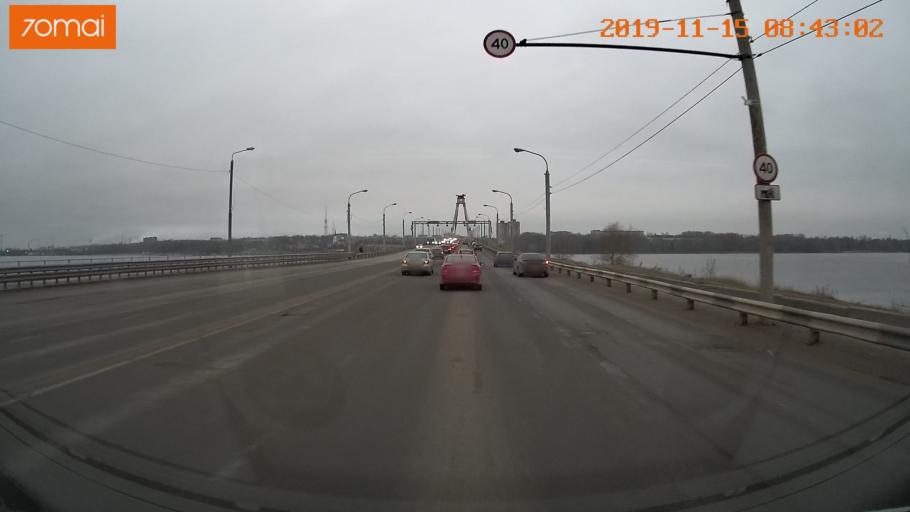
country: RU
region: Vologda
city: Cherepovets
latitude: 59.1068
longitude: 37.9055
